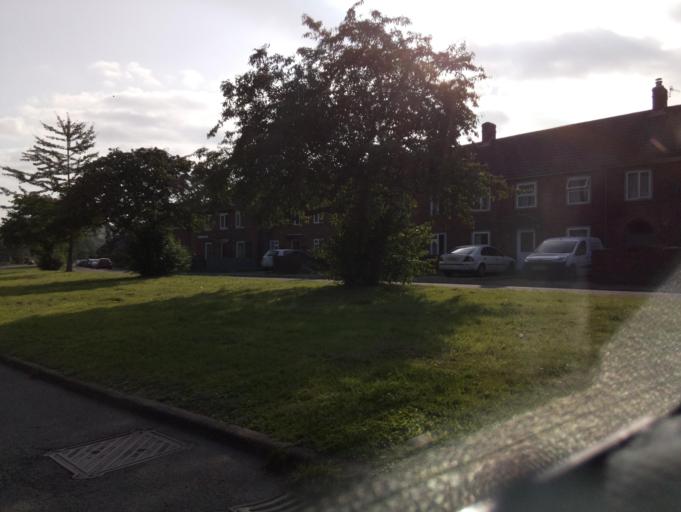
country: GB
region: England
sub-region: Devon
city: Tiverton
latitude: 50.8982
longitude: -3.4902
